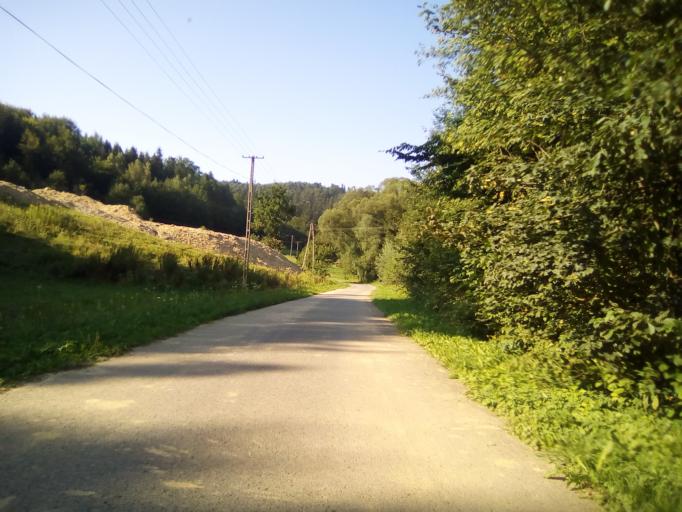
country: PL
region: Subcarpathian Voivodeship
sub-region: Powiat brzozowski
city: Domaradz
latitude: 49.8119
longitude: 21.9447
